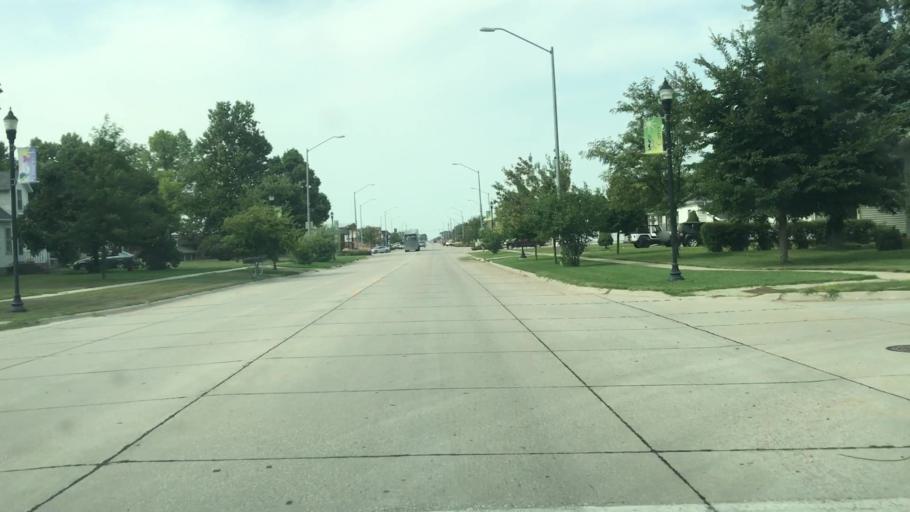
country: US
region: Nebraska
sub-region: Hall County
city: Wood River
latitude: 40.9980
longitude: -98.6075
